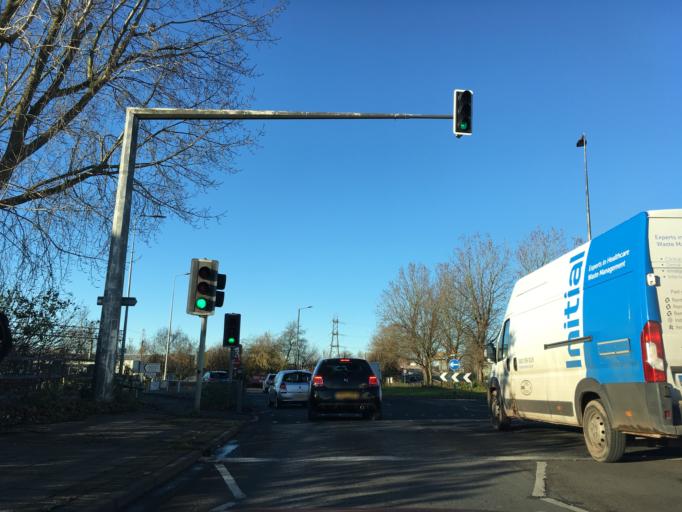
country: GB
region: England
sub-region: Bristol
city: Bristol
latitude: 51.4457
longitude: -2.5604
